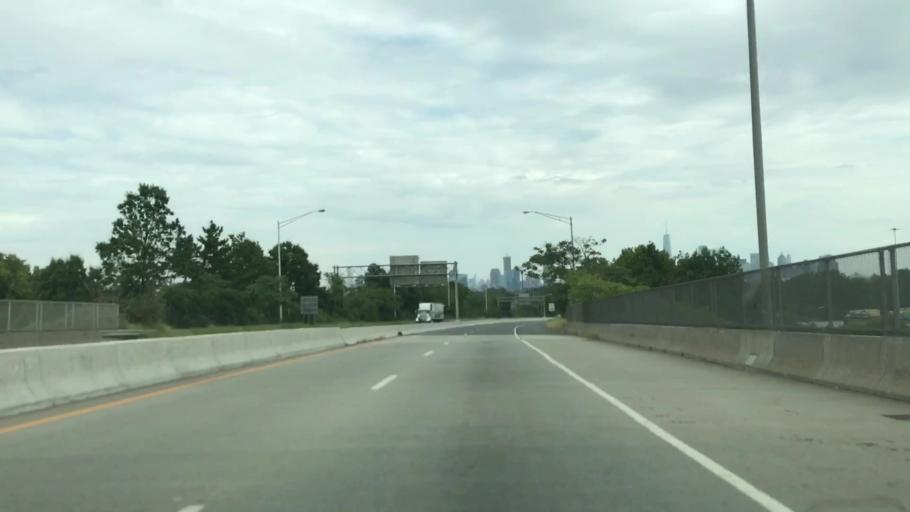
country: US
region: New Jersey
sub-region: Hudson County
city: Bayonne
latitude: 40.6858
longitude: -74.0907
